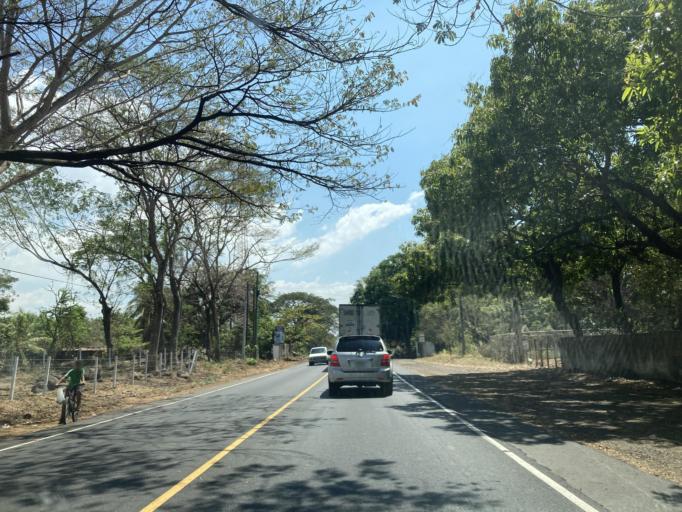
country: GT
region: Santa Rosa
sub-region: Municipio de Taxisco
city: Taxisco
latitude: 14.0922
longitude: -90.5672
